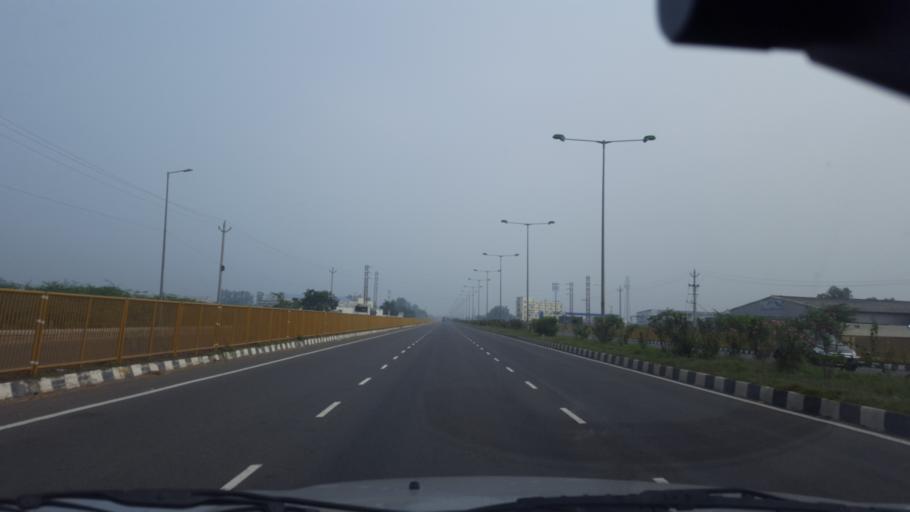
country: IN
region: Andhra Pradesh
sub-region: Guntur
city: Chilakalurupet
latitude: 15.9961
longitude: 80.1090
